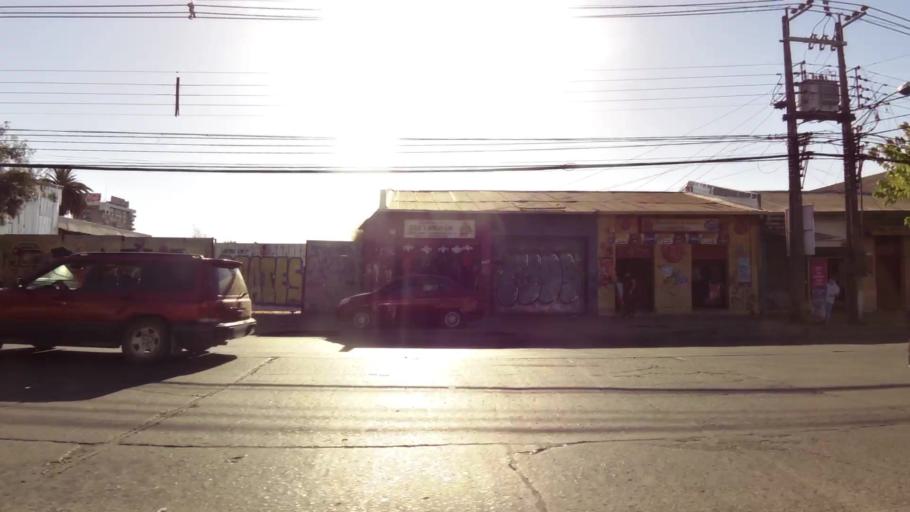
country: CL
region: Maule
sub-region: Provincia de Talca
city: Talca
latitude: -35.4264
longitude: -71.6501
